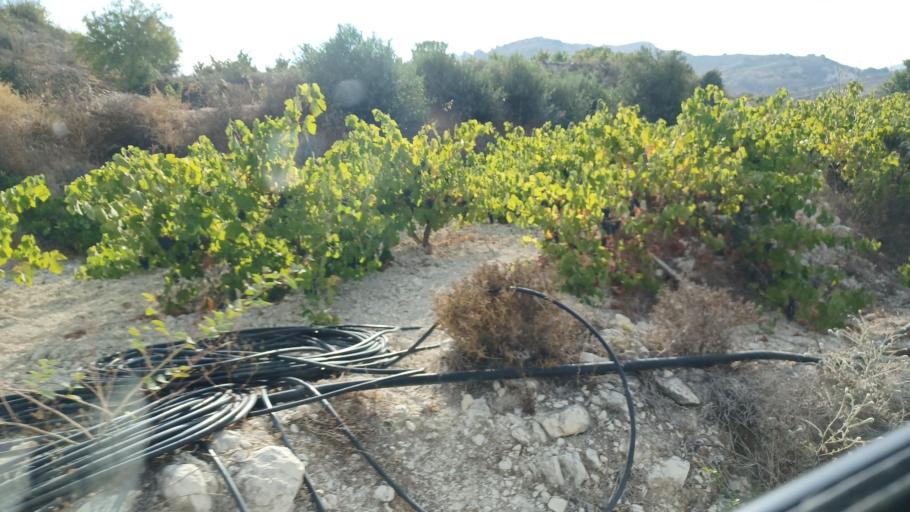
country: CY
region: Pafos
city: Tala
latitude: 34.8818
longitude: 32.4530
